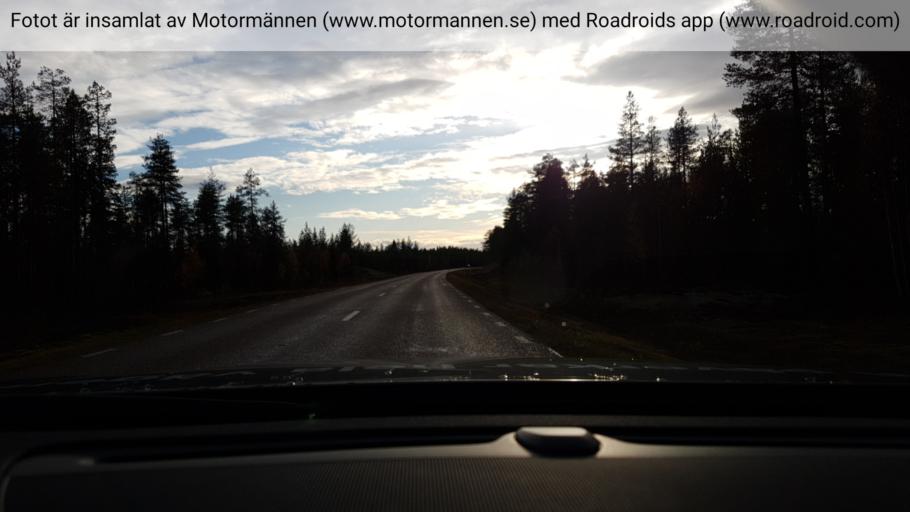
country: SE
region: Norrbotten
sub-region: Pajala Kommun
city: Pajala
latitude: 67.1737
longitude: 22.6884
